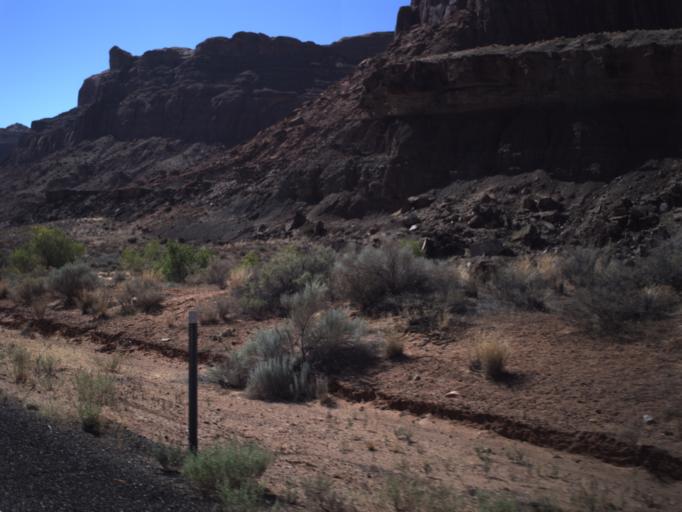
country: US
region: Utah
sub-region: San Juan County
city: Blanding
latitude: 37.9180
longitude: -110.4626
